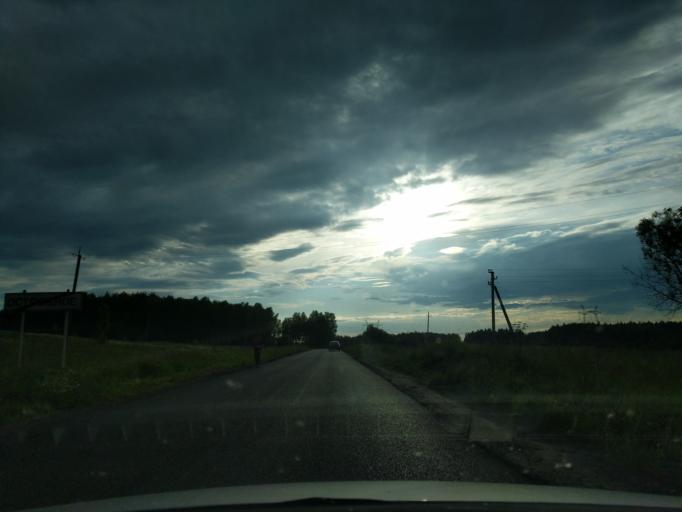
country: RU
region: Kaluga
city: Myatlevo
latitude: 54.8017
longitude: 35.7166
